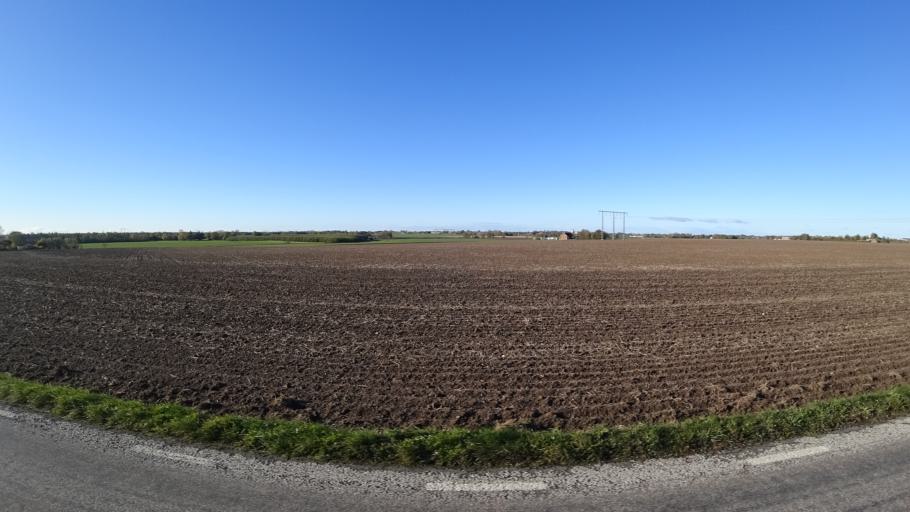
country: SE
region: Skane
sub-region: Staffanstorps Kommun
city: Staffanstorp
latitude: 55.6742
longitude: 13.2326
